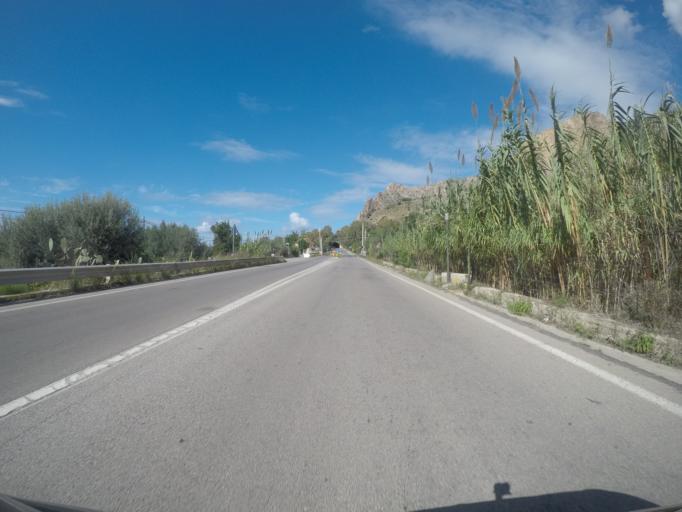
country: IT
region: Sicily
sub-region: Palermo
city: Agliandroni-Paternella
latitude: 38.1207
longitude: 13.0761
